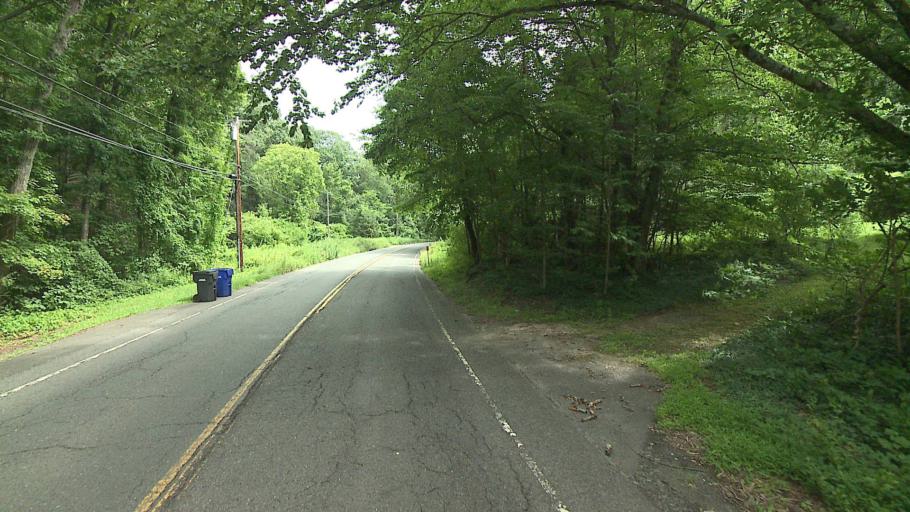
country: US
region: Connecticut
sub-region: Fairfield County
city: Sherman
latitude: 41.6438
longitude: -73.4946
